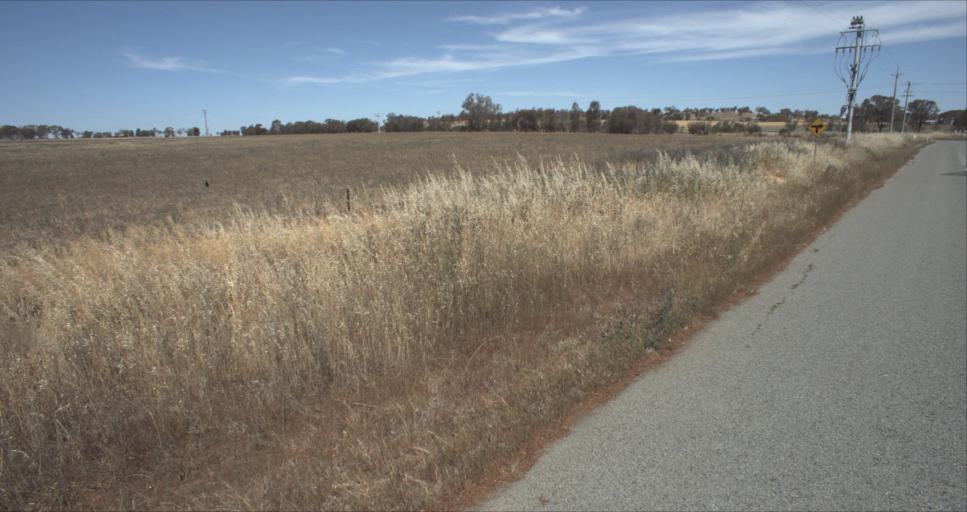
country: AU
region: New South Wales
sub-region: Leeton
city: Leeton
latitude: -34.6140
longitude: 146.4340
